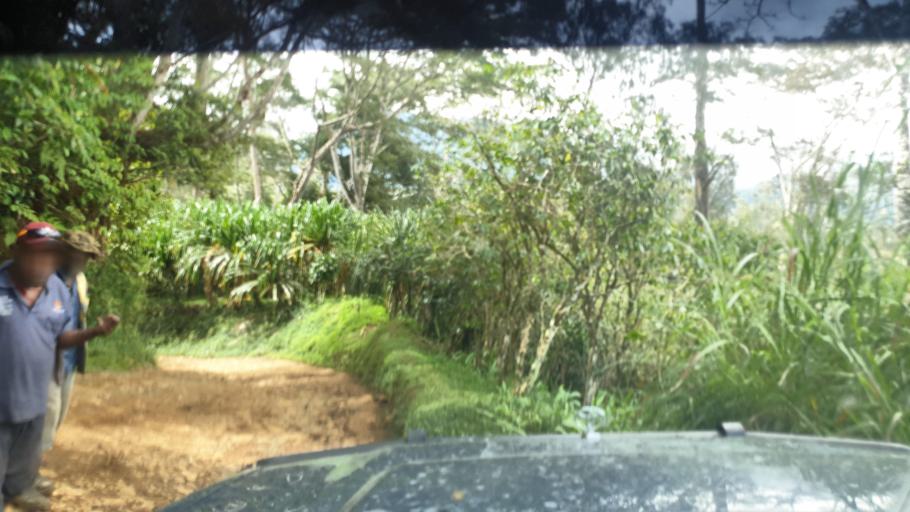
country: PG
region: Jiwaka
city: Minj
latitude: -5.8945
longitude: 144.8153
